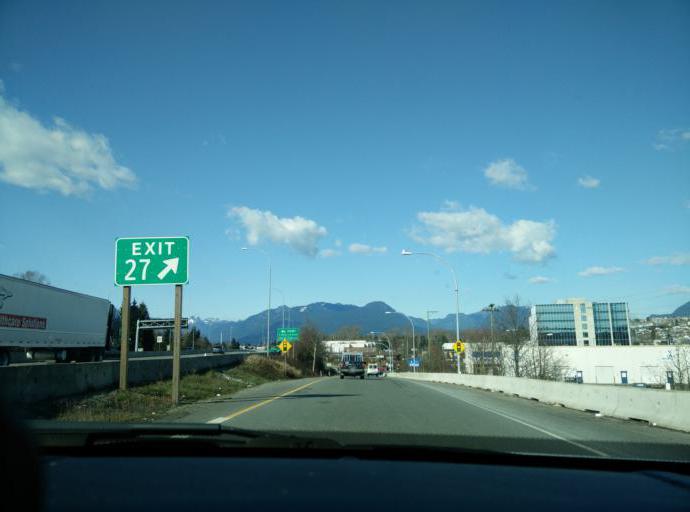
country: CA
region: British Columbia
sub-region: Fraser Valley Regional District
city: North Vancouver
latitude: 49.2679
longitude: -123.0265
